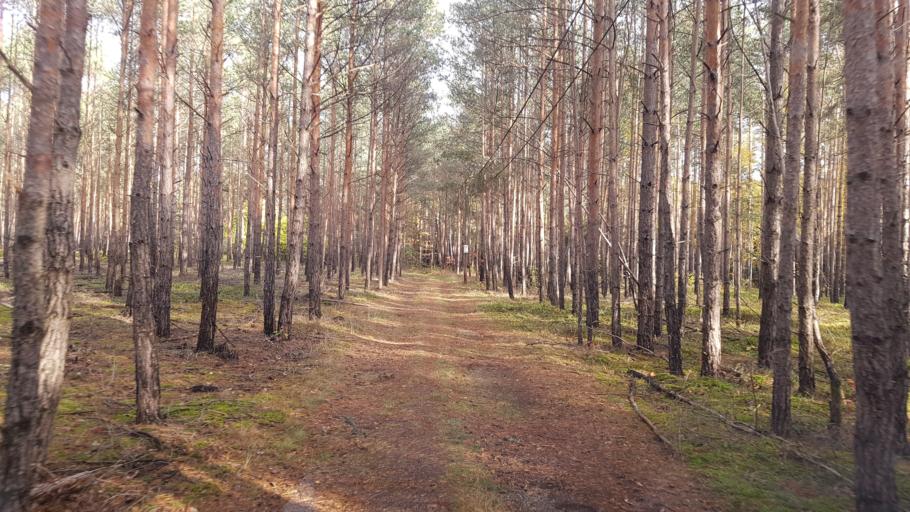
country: DE
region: Brandenburg
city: Finsterwalde
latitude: 51.5817
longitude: 13.7059
